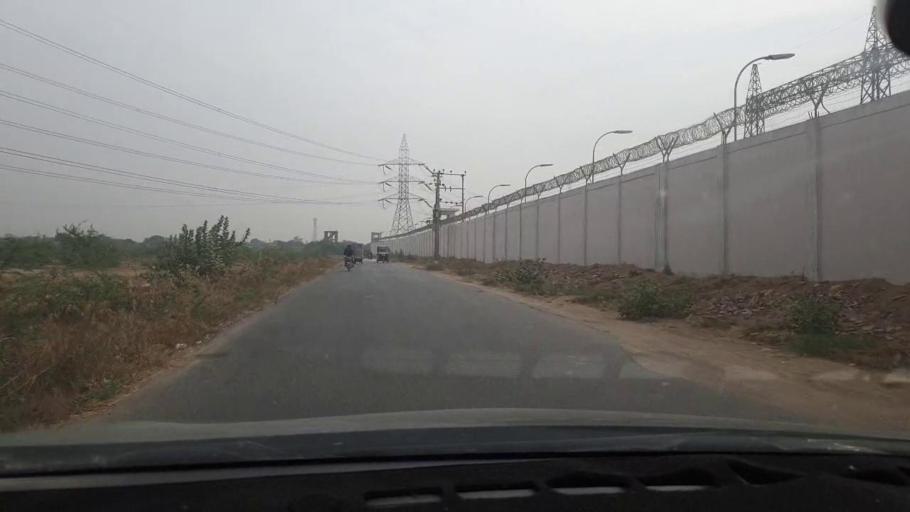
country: PK
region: Sindh
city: Malir Cantonment
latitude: 24.9115
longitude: 67.2832
